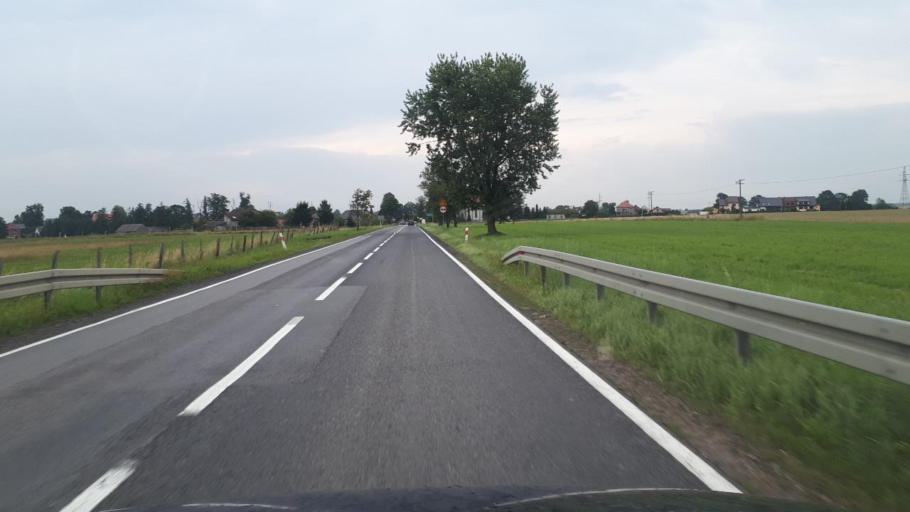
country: PL
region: Opole Voivodeship
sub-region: Powiat oleski
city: Olesno
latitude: 50.8450
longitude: 18.4877
